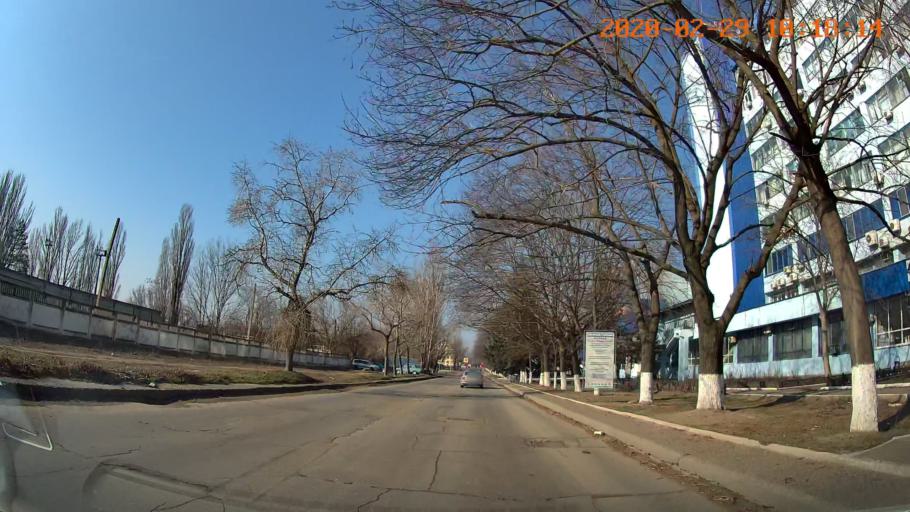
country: MD
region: Telenesti
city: Tiraspolul Nou
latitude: 46.8558
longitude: 29.6159
